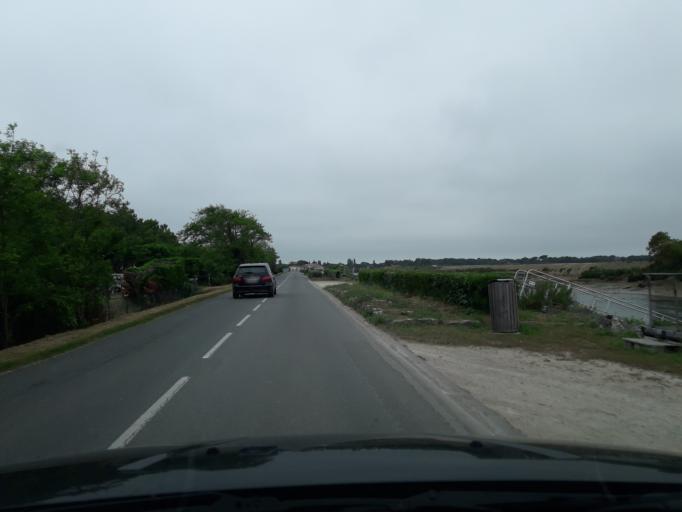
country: FR
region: Poitou-Charentes
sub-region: Departement de la Charente-Maritime
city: Boyard-Ville
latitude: 45.9630
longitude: -1.2459
